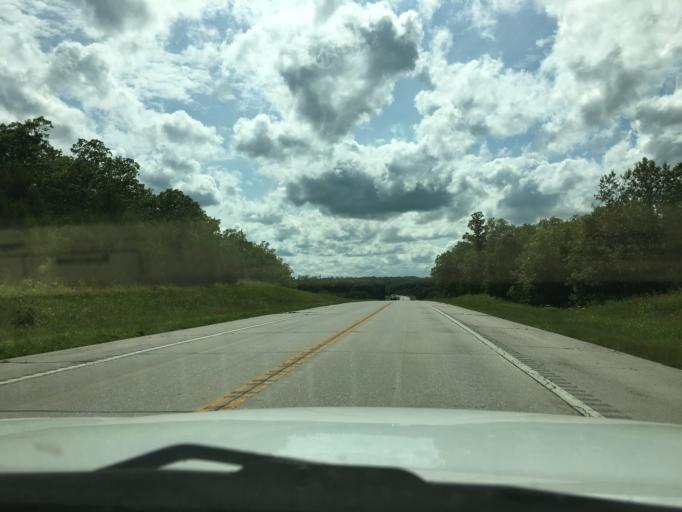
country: US
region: Missouri
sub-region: Franklin County
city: Gerald
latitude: 38.4236
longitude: -91.2681
